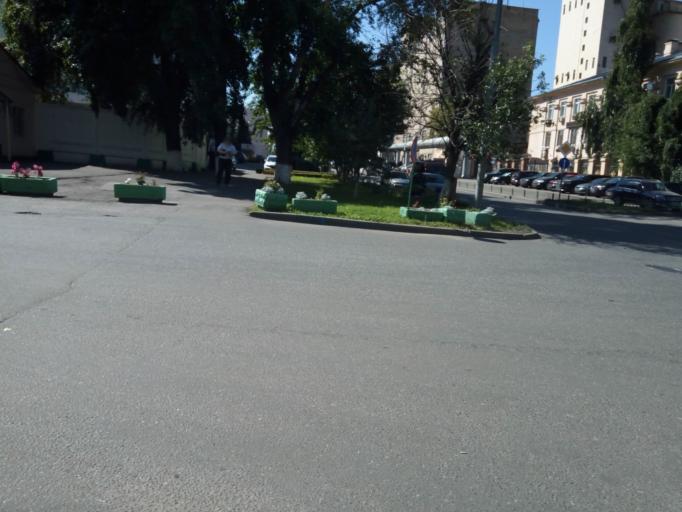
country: RU
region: Moscow
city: Sokol
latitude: 55.7716
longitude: 37.5254
